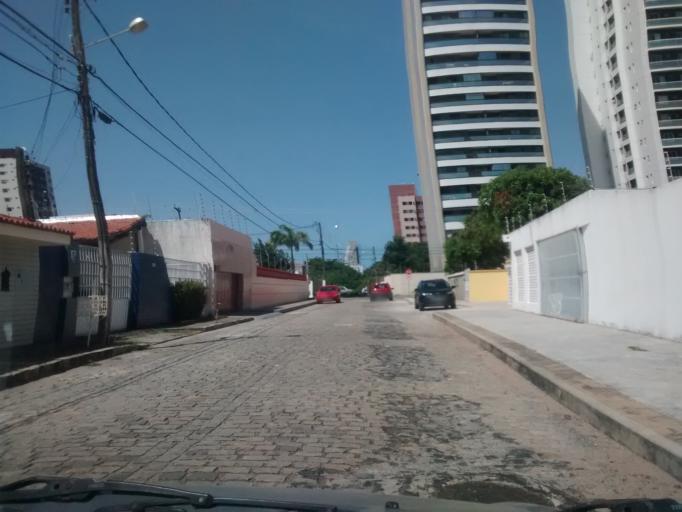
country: BR
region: Rio Grande do Norte
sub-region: Natal
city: Natal
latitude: -5.8209
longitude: -35.2174
